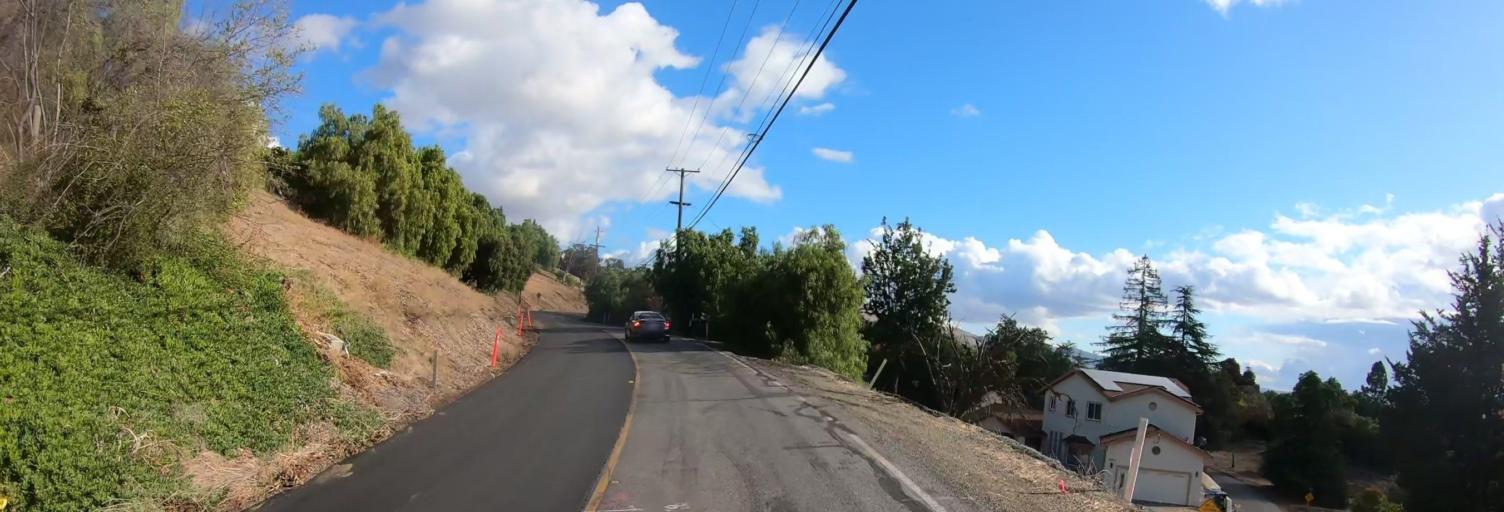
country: US
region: California
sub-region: Santa Clara County
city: East Foothills
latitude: 37.3787
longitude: -121.8099
